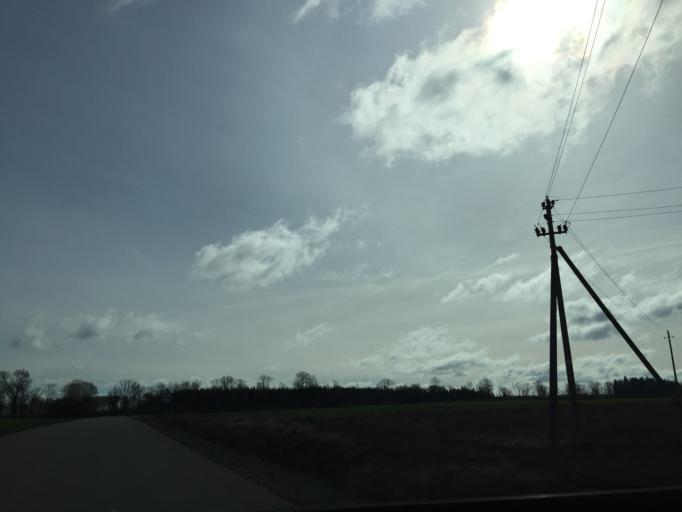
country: LT
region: Siauliu apskritis
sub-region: Joniskis
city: Joniskis
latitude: 56.1808
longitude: 23.5352
